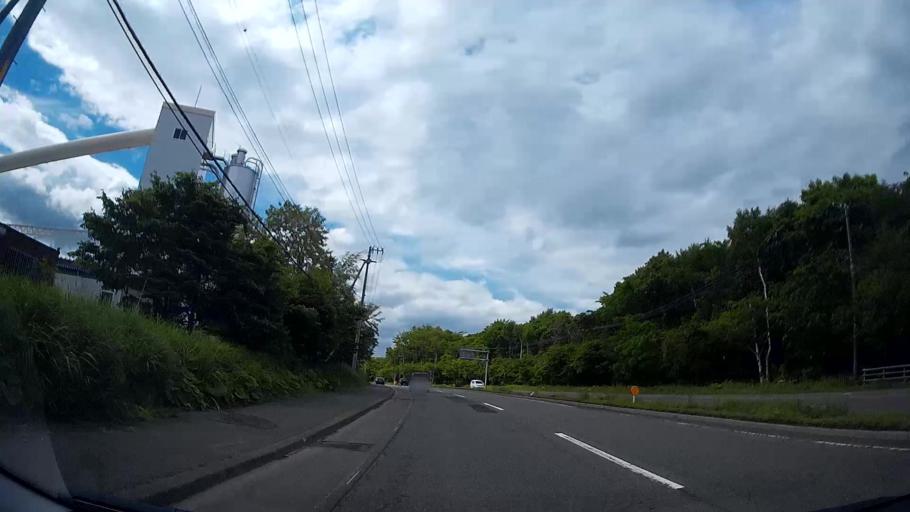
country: JP
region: Hokkaido
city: Chitose
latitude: 42.8562
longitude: 141.6084
